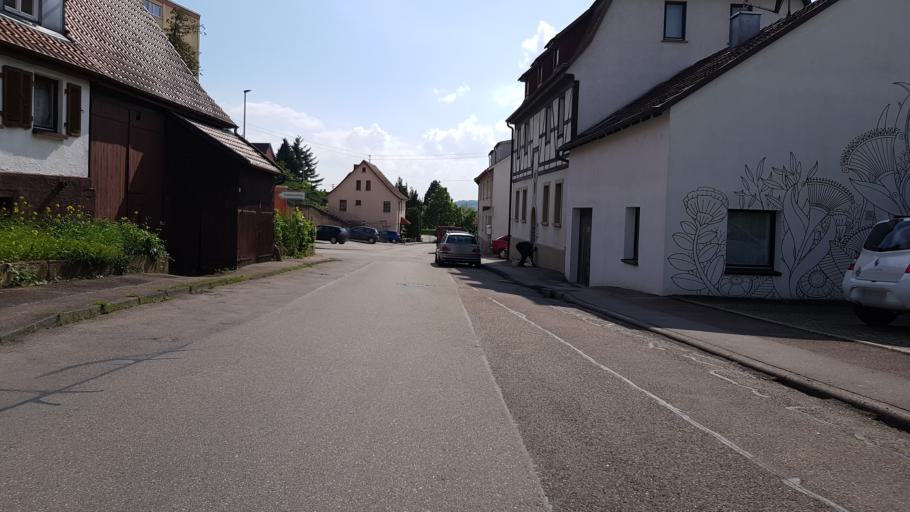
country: DE
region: Baden-Wuerttemberg
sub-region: Regierungsbezirk Stuttgart
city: Steinheim am der Murr
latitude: 48.9680
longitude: 9.2829
